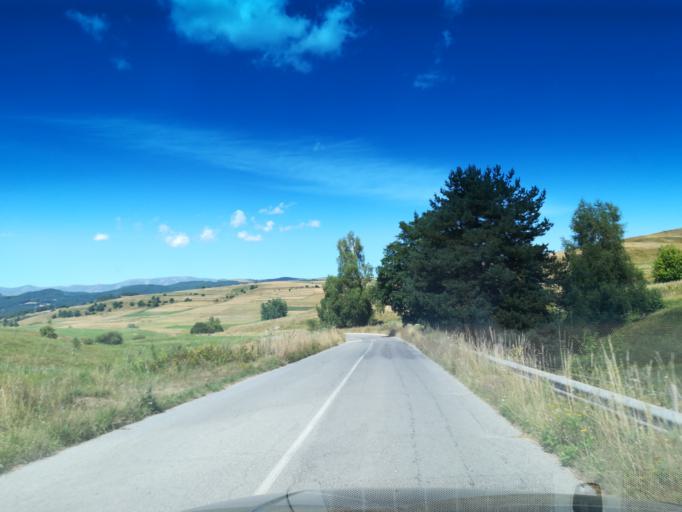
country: BG
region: Sofiya
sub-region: Obshtina Koprivshtitsa
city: Koprivshtitsa
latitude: 42.5990
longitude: 24.3791
